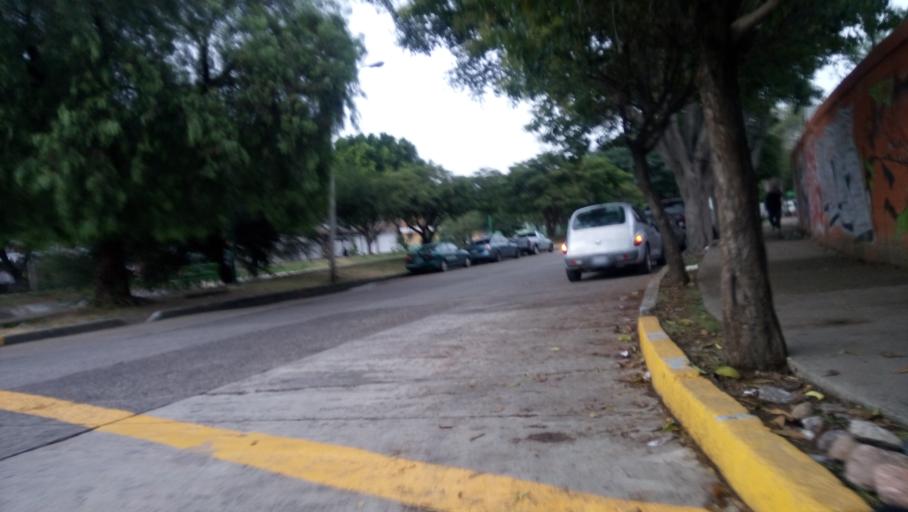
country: MX
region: Guanajuato
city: Leon
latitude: 21.1420
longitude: -101.6655
